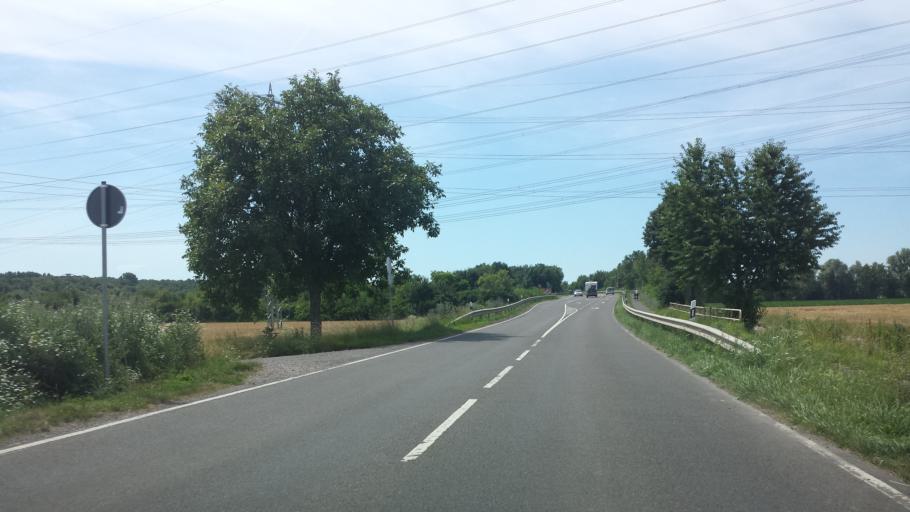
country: DE
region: Rheinland-Pfalz
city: Osthofen
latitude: 49.6798
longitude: 8.3289
